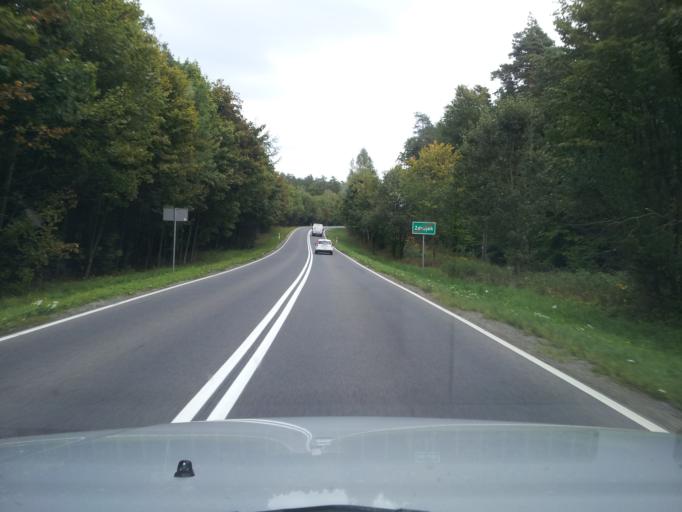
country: PL
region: Warmian-Masurian Voivodeship
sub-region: Powiat olsztynski
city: Gietrzwald
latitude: 53.7311
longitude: 20.1643
